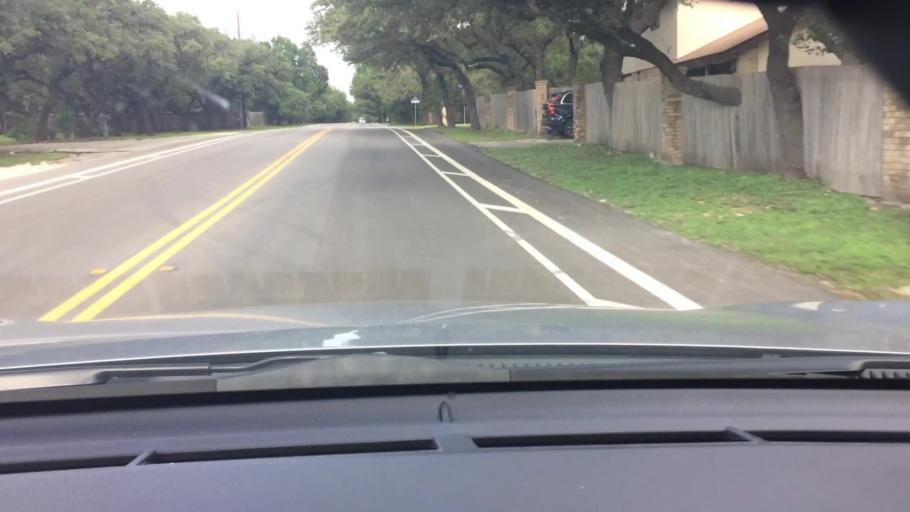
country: US
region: Texas
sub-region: Bexar County
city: Shavano Park
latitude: 29.5577
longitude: -98.5470
